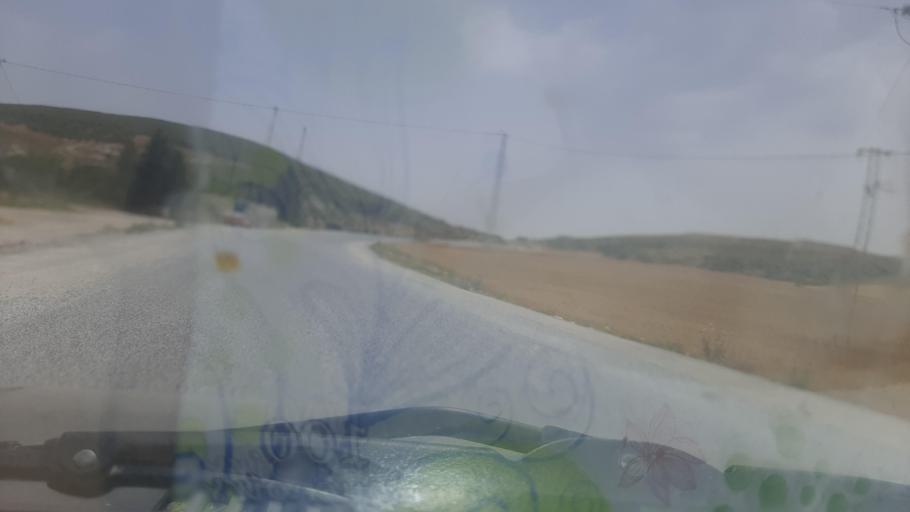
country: TN
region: Zaghwan
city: Zaghouan
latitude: 36.5368
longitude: 10.1541
